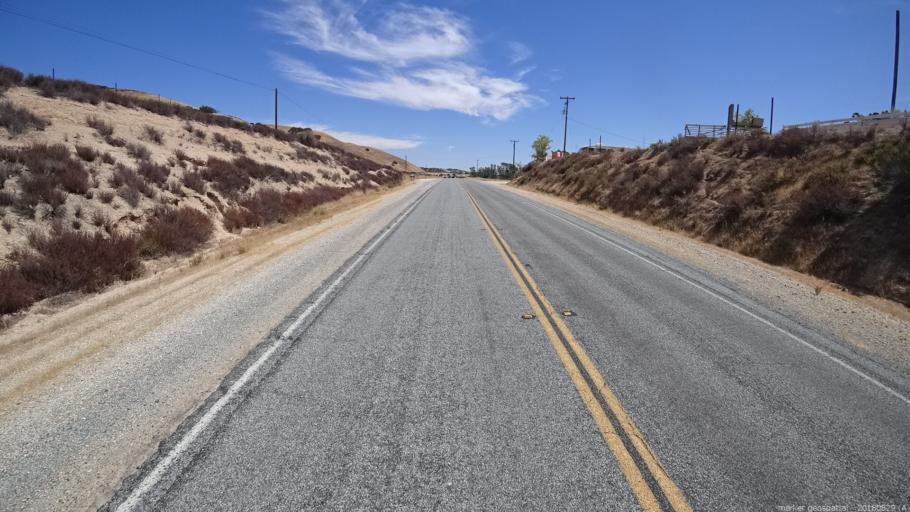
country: US
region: California
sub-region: San Luis Obispo County
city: Lake Nacimiento
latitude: 35.9163
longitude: -121.0278
